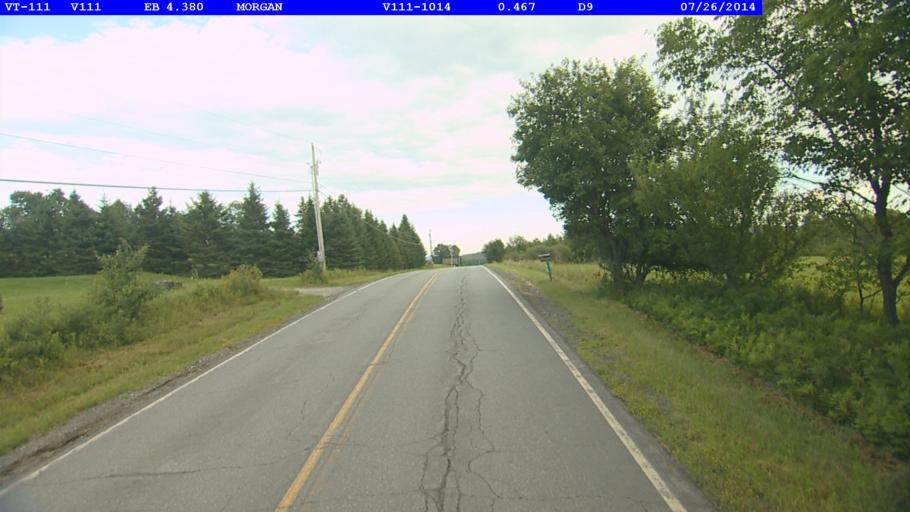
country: US
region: Vermont
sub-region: Orleans County
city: Newport
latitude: 44.9268
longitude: -72.0566
